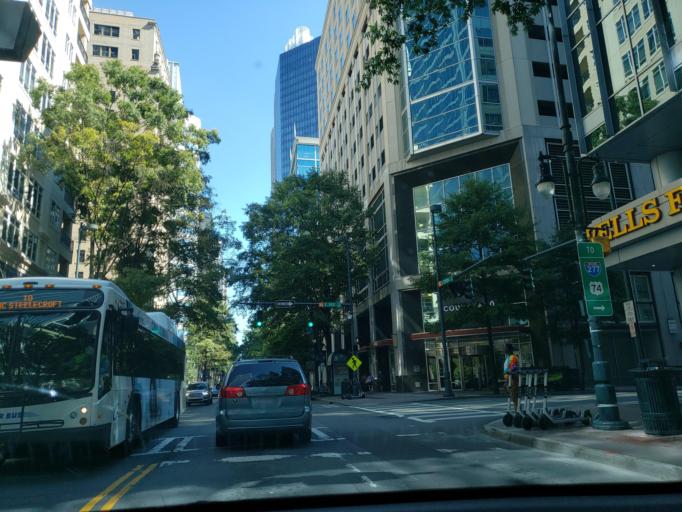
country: US
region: North Carolina
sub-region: Mecklenburg County
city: Charlotte
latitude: 35.2256
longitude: -80.8456
